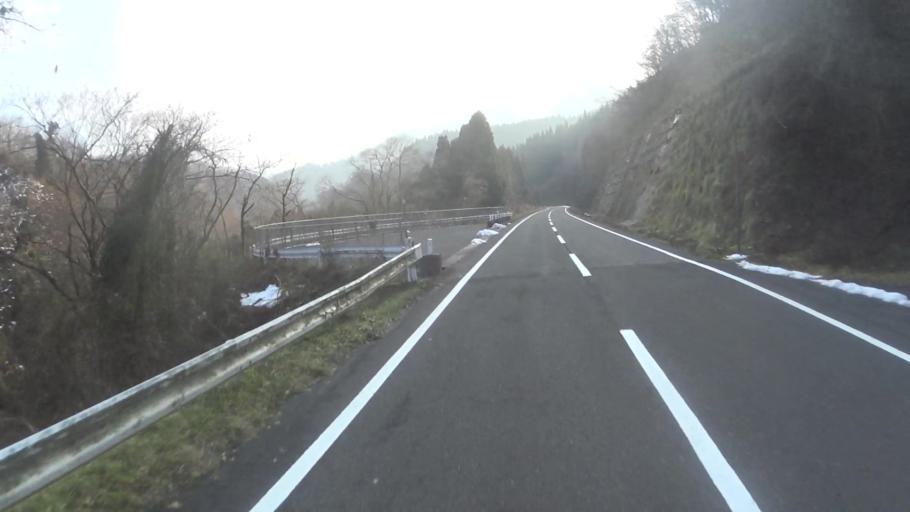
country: JP
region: Kyoto
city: Maizuru
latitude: 35.4203
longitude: 135.4096
